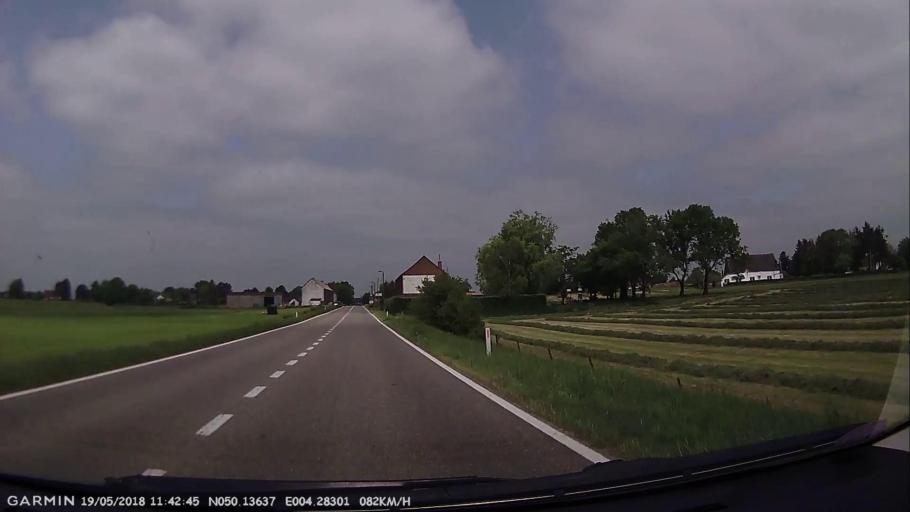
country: BE
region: Wallonia
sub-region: Province du Hainaut
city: Froidchapelle
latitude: 50.1366
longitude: 4.2828
